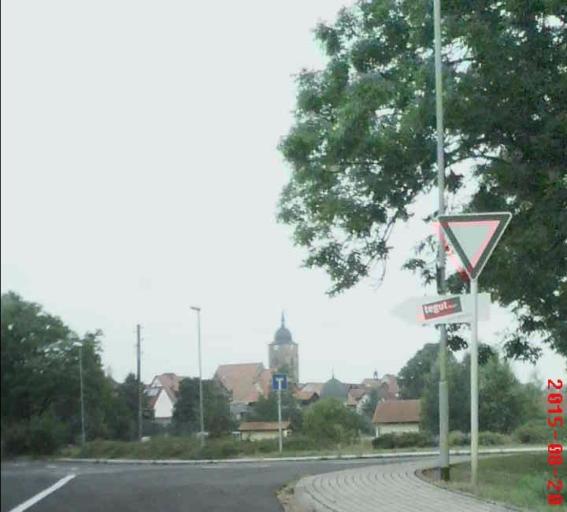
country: DE
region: Thuringia
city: Hellingen
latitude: 50.2778
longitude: 10.7319
